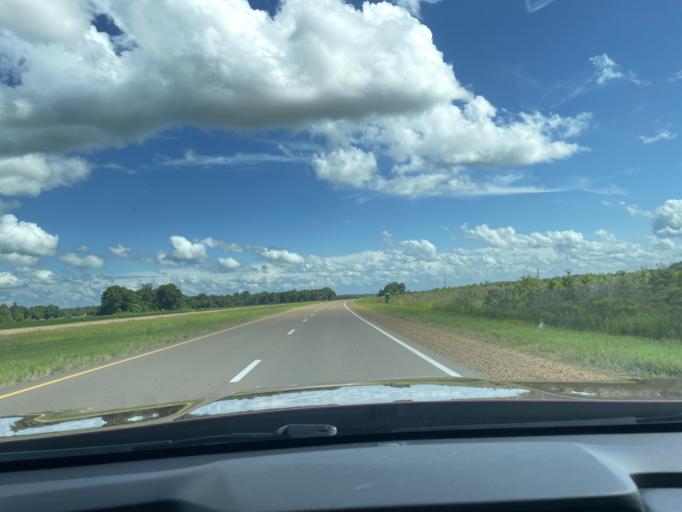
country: US
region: Mississippi
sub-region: Humphreys County
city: Belzoni
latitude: 33.0461
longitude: -90.4673
